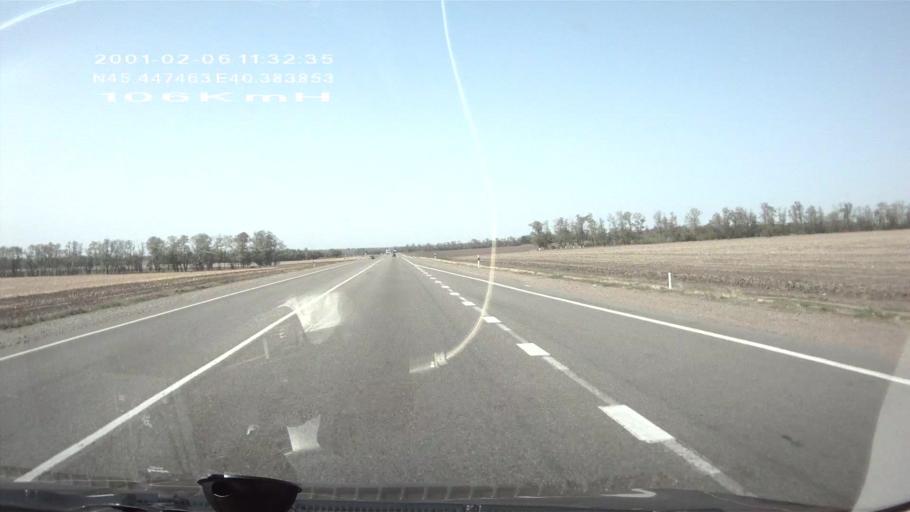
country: RU
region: Krasnodarskiy
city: Kazanskaya
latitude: 45.4471
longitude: 40.3820
